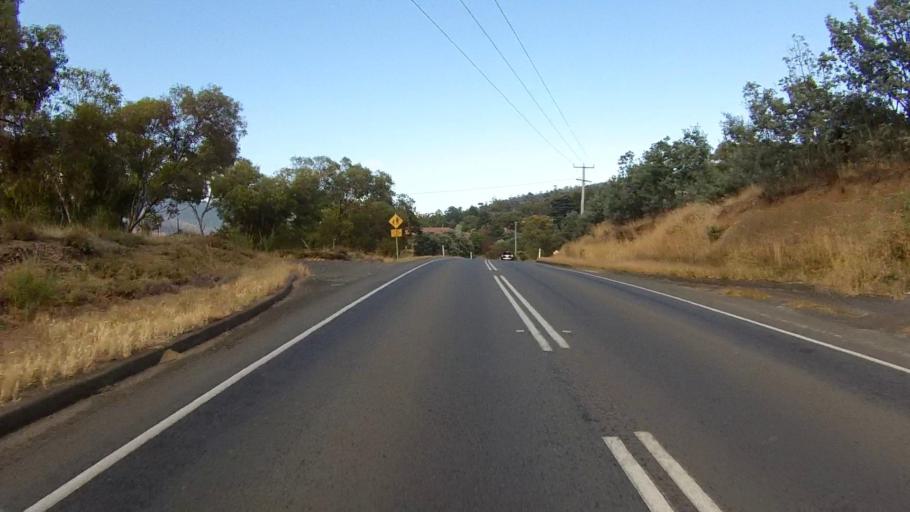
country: AU
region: Tasmania
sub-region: Brighton
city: Bridgewater
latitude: -42.7288
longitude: 147.1811
